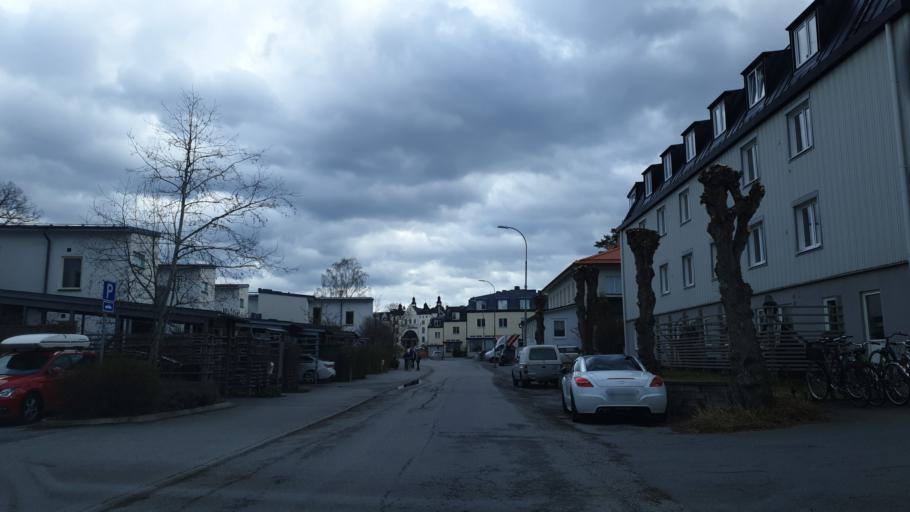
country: SE
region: Stockholm
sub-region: Nacka Kommun
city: Saltsjobaden
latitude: 59.2795
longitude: 18.3080
